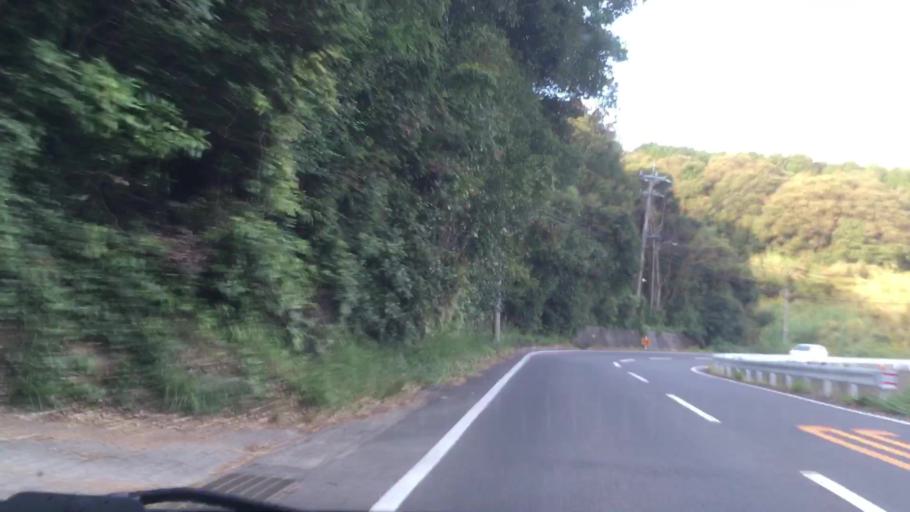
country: JP
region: Nagasaki
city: Sasebo
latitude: 32.9571
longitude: 129.6785
